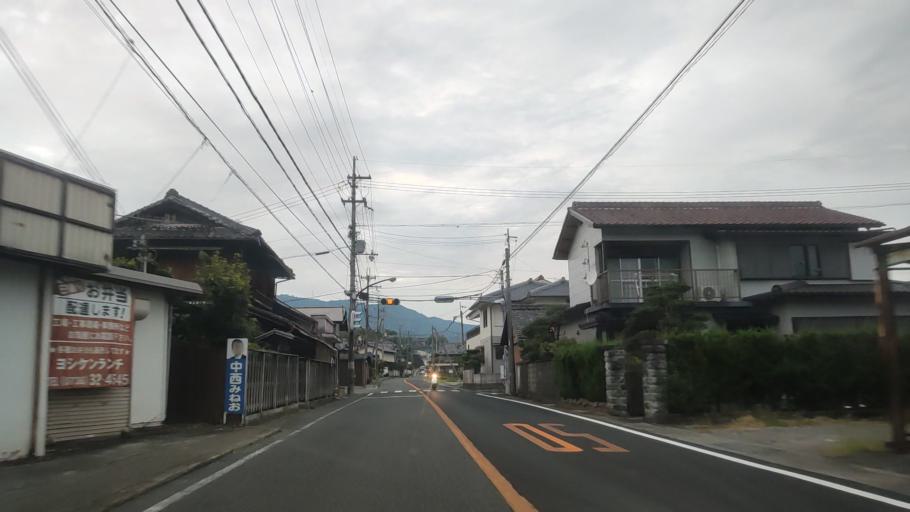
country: JP
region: Wakayama
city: Hashimoto
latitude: 34.3313
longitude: 135.6069
